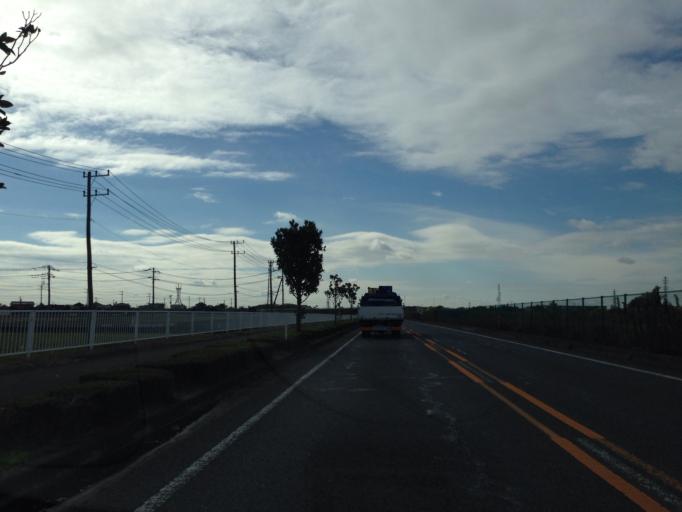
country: JP
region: Ibaraki
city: Fujishiro
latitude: 35.9307
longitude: 140.1191
